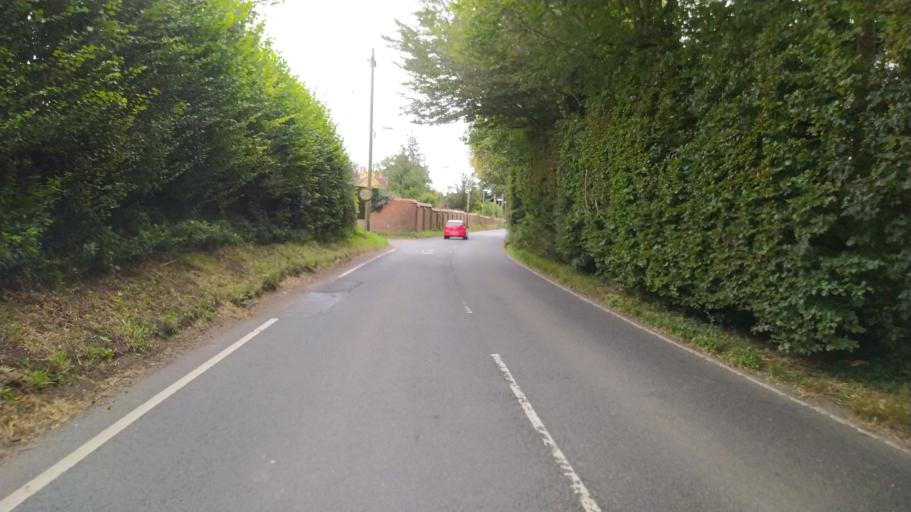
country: GB
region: England
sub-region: Dorset
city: Gillingham
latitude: 51.0401
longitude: -2.3002
